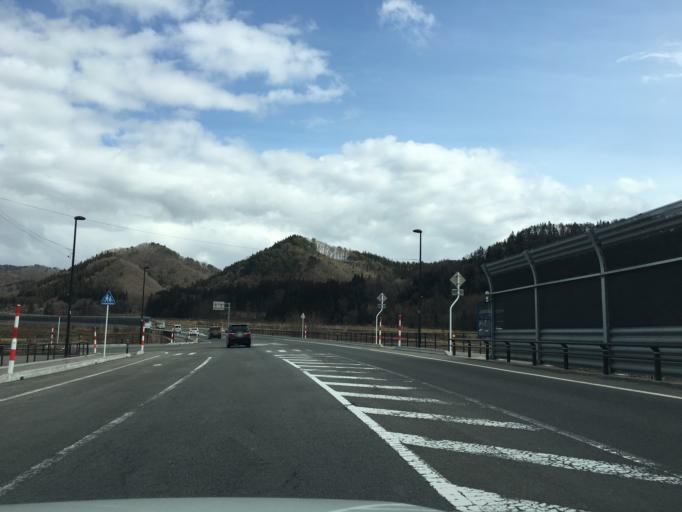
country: JP
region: Akita
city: Hanawa
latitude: 40.2236
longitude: 140.7185
